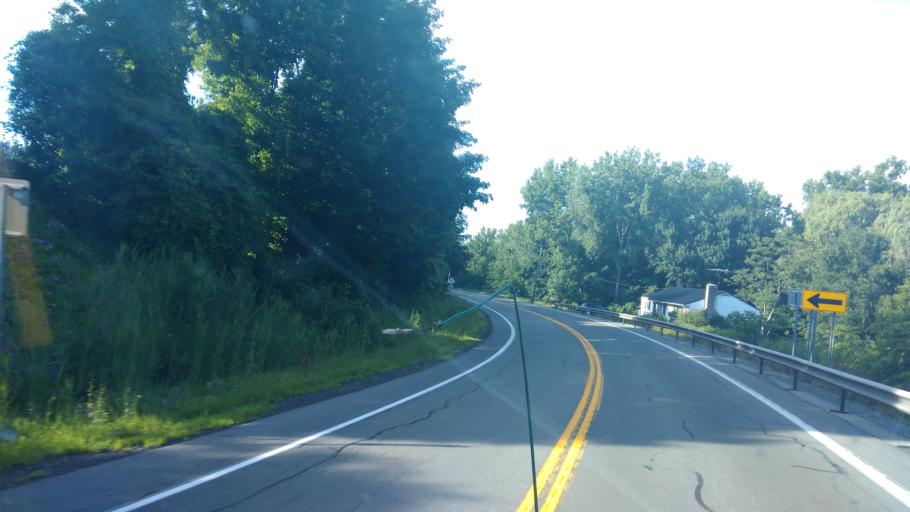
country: US
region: New York
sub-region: Wayne County
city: Lyons
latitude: 43.0847
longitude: -76.9861
